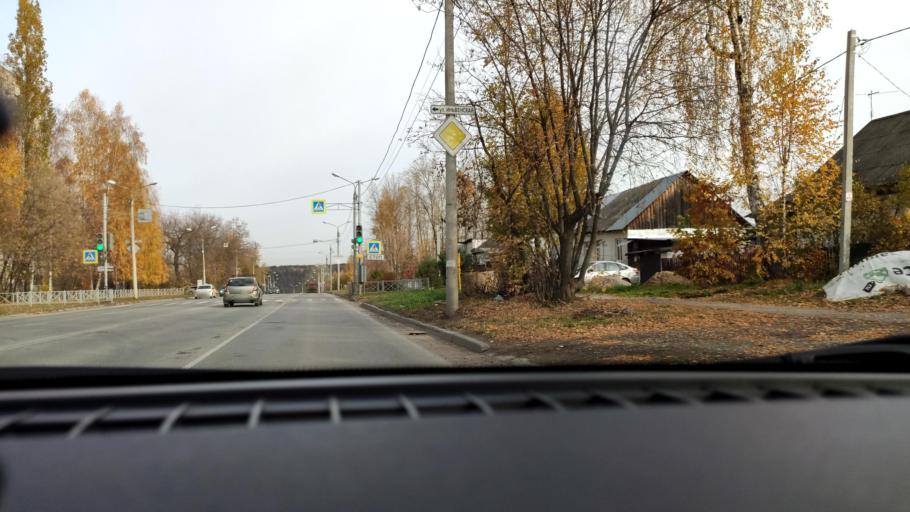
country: RU
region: Perm
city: Perm
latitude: 58.0633
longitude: 56.3631
